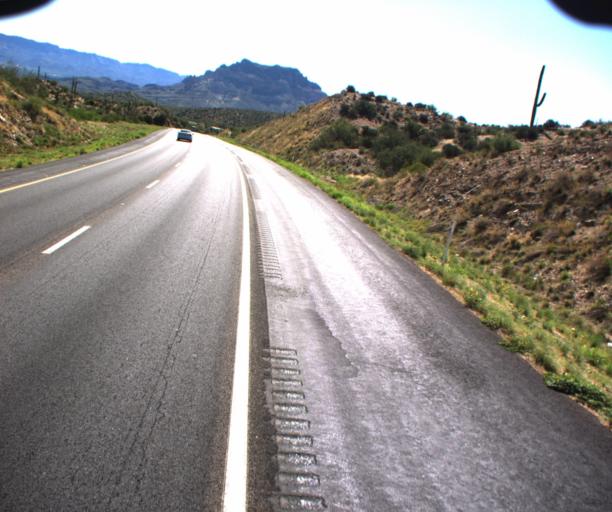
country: US
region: Arizona
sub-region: Pinal County
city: Gold Camp
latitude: 33.2741
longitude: -111.2248
